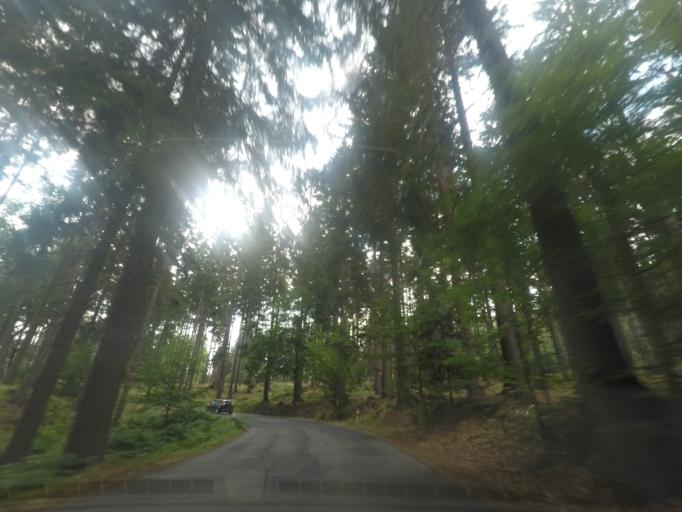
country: CZ
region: Ustecky
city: Mikulasovice
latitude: 50.8688
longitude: 14.3312
